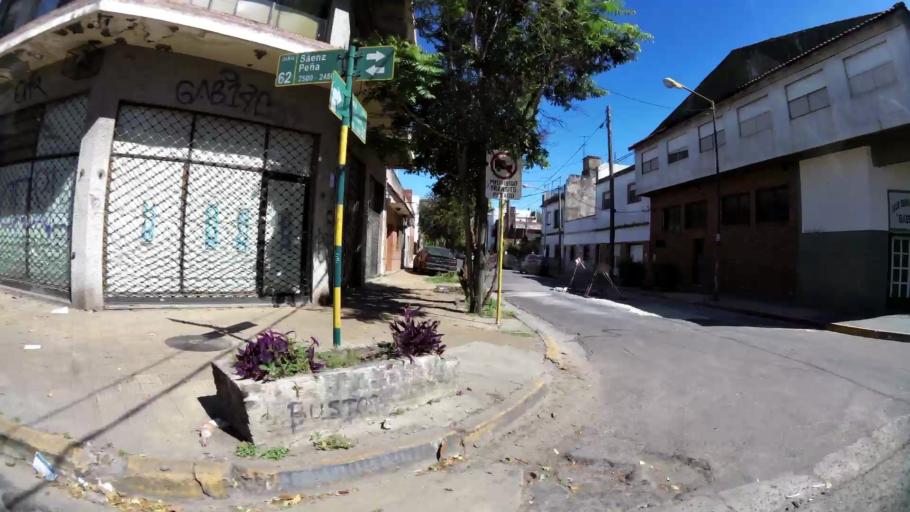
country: AR
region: Buenos Aires
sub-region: Partido de General San Martin
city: General San Martin
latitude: -34.5641
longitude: -58.5308
